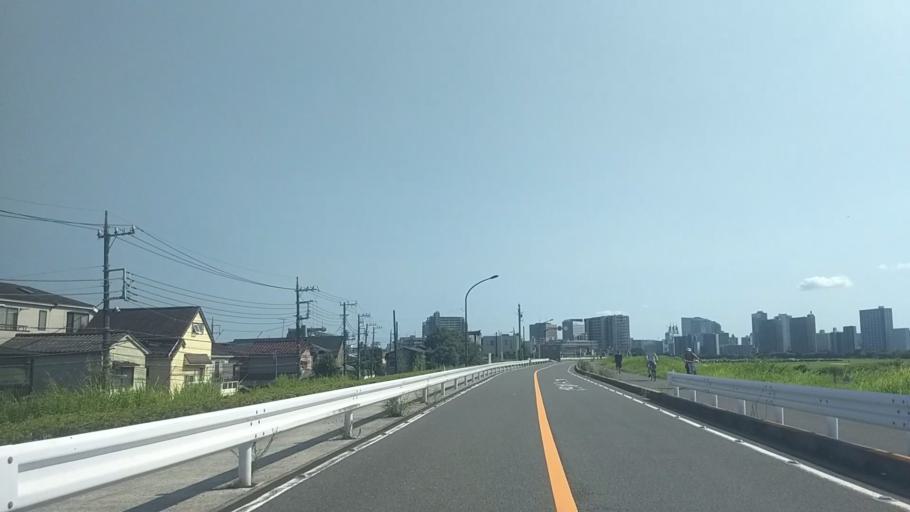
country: JP
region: Kanagawa
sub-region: Kawasaki-shi
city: Kawasaki
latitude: 35.5513
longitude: 139.7053
